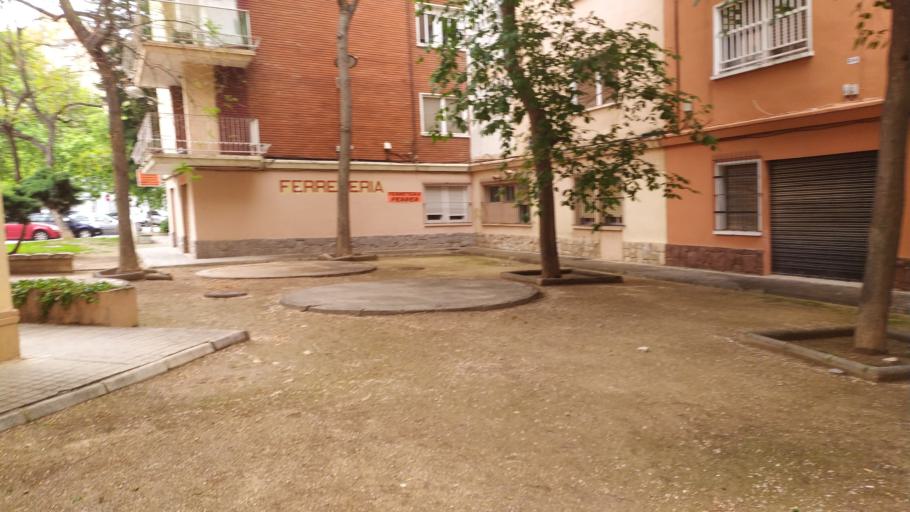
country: ES
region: Valencia
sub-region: Provincia de Valencia
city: Mislata
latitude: 39.4678
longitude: -0.4150
